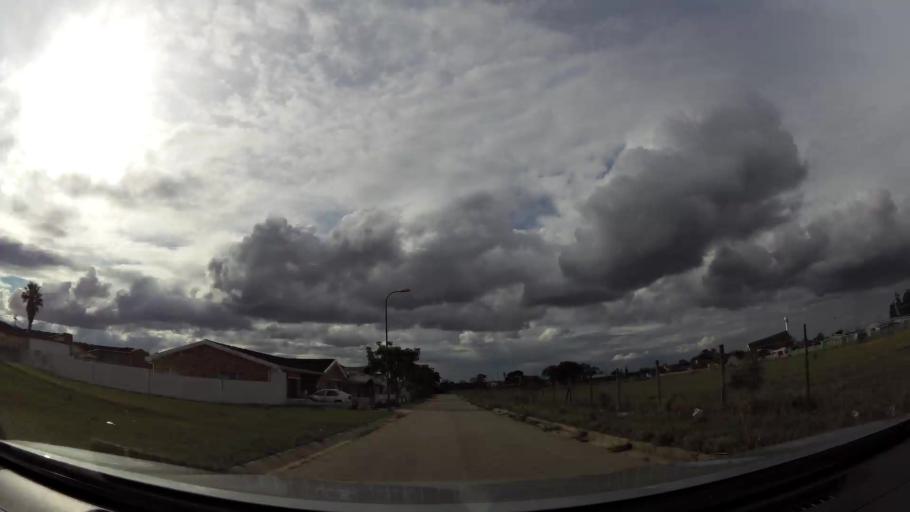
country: ZA
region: Eastern Cape
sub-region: Nelson Mandela Bay Metropolitan Municipality
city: Port Elizabeth
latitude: -33.9389
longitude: 25.5063
